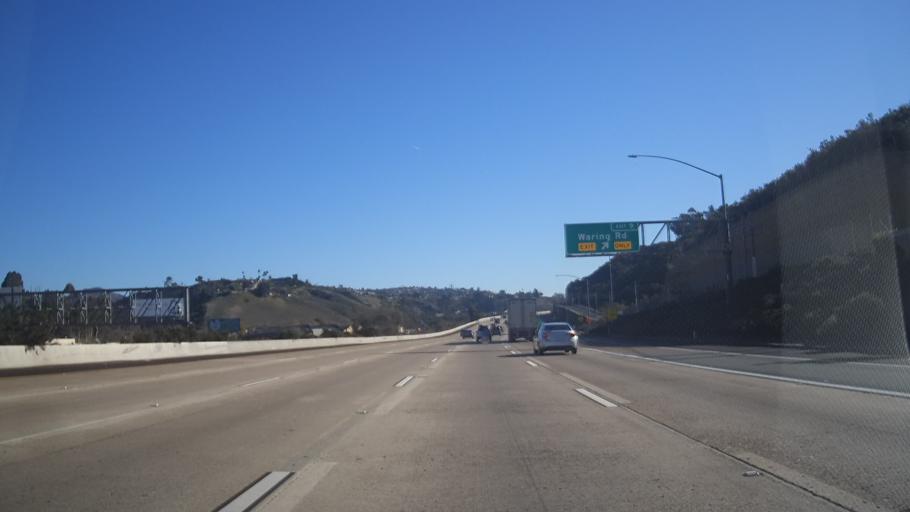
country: US
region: California
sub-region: San Diego County
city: La Mesa
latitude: 32.7796
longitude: -117.0940
